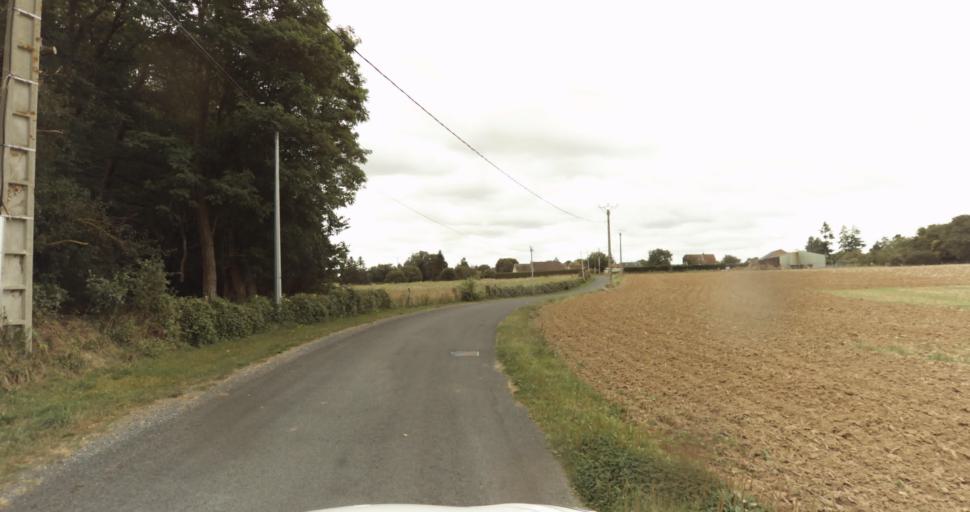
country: FR
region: Haute-Normandie
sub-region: Departement de l'Eure
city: Nonancourt
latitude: 48.8159
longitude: 1.1730
